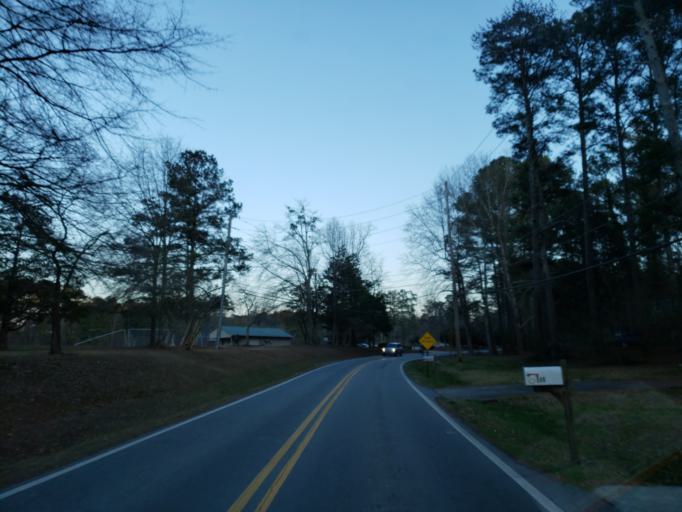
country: US
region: Georgia
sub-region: Cherokee County
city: Woodstock
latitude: 34.1056
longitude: -84.4962
